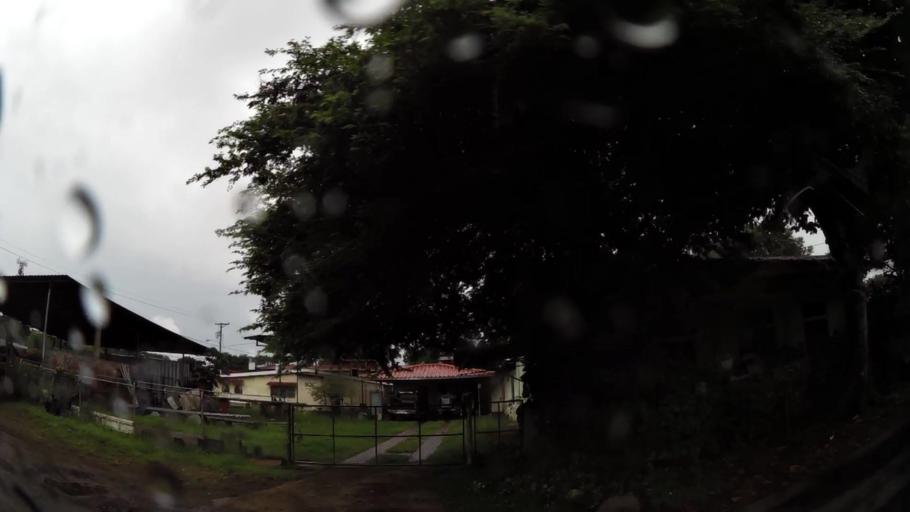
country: PA
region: Chiriqui
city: David
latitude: 8.4315
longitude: -82.4352
